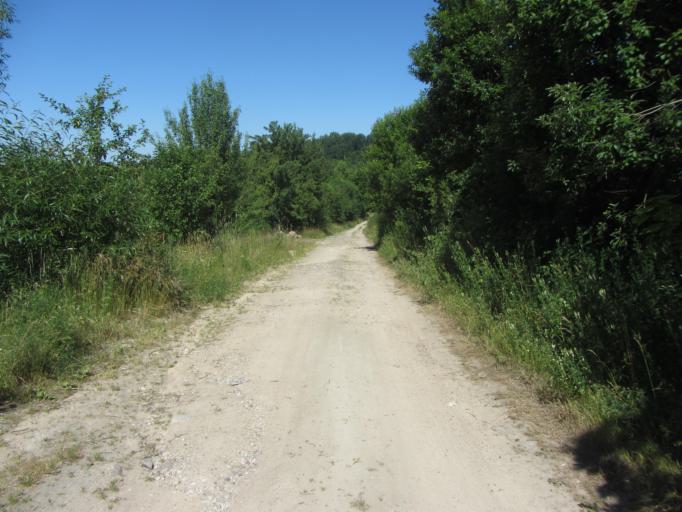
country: LT
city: Aukstadvaris
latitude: 54.5752
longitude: 24.3872
